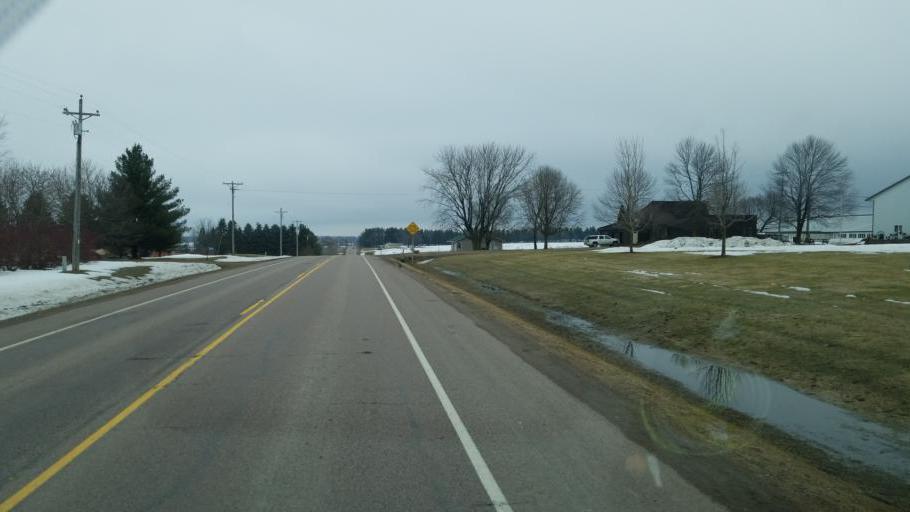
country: US
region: Wisconsin
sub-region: Wood County
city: Marshfield
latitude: 44.6422
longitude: -90.2184
